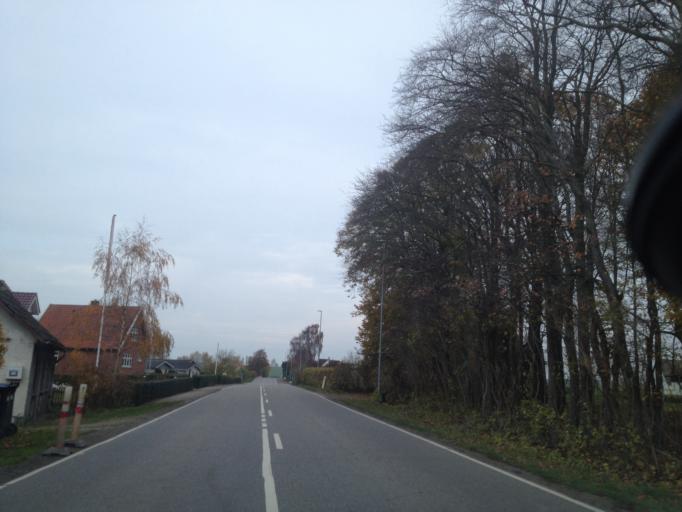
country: DK
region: South Denmark
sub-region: Nordfyns Kommune
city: Bogense
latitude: 55.5026
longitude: 10.0972
